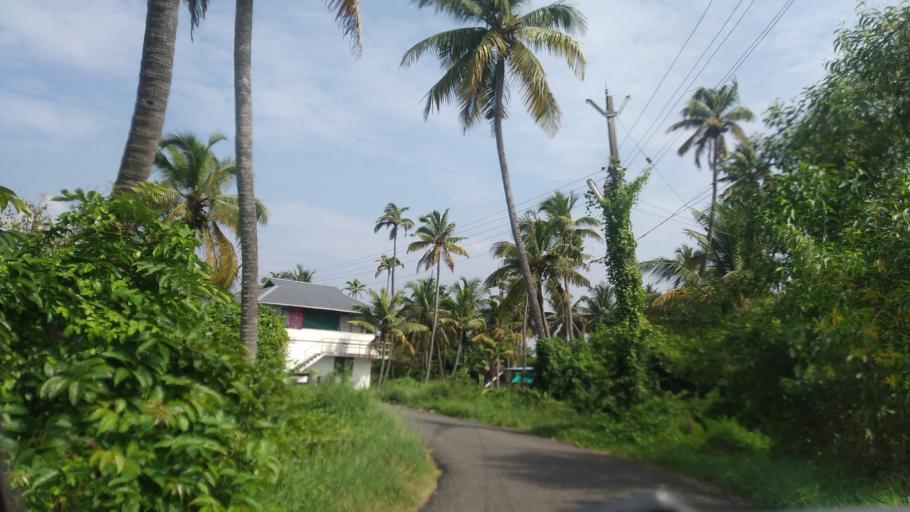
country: IN
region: Kerala
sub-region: Ernakulam
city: Elur
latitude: 10.0864
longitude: 76.1980
